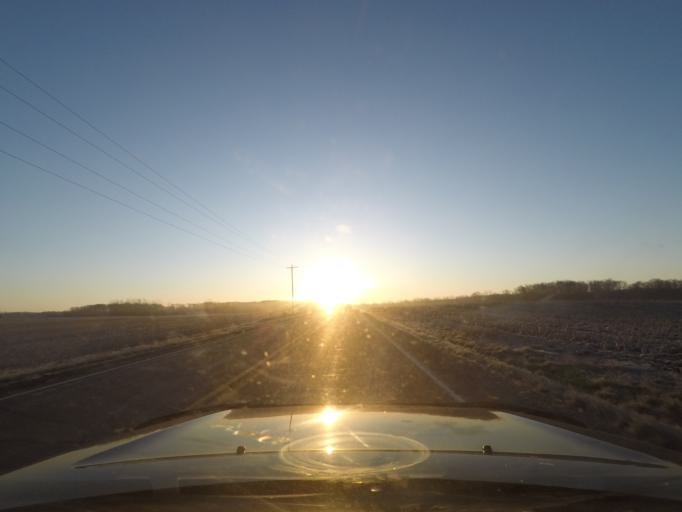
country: US
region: Indiana
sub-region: Marshall County
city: Plymouth
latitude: 41.4488
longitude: -86.3482
